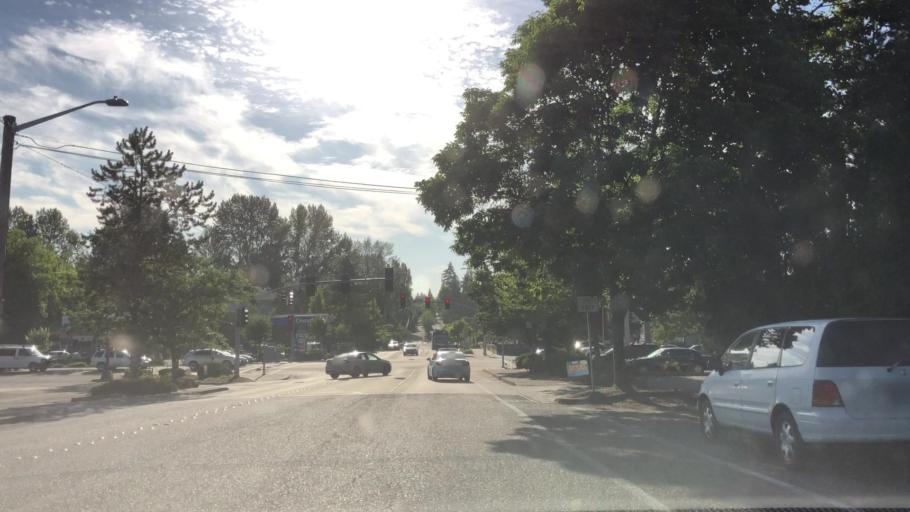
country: US
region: Washington
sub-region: King County
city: Eastgate
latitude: 47.6098
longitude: -122.1442
